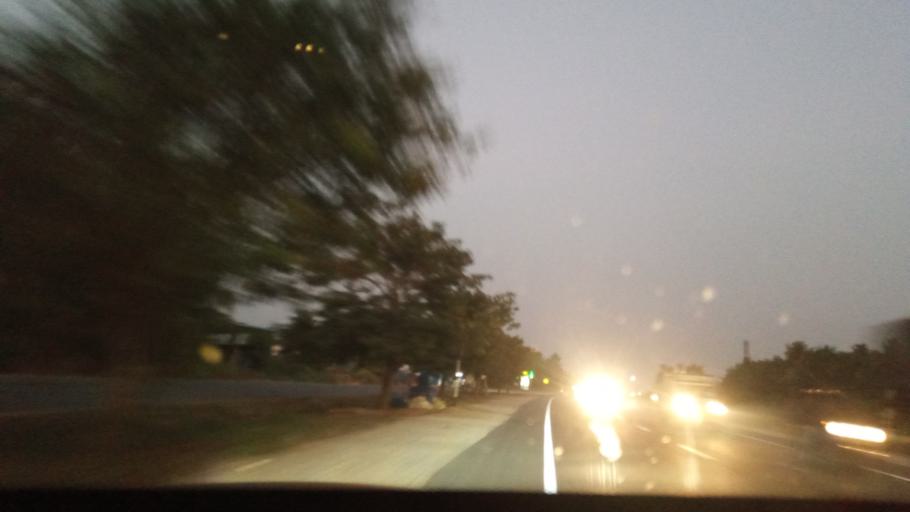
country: IN
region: Tamil Nadu
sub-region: Salem
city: Attur
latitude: 11.6137
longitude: 78.5783
